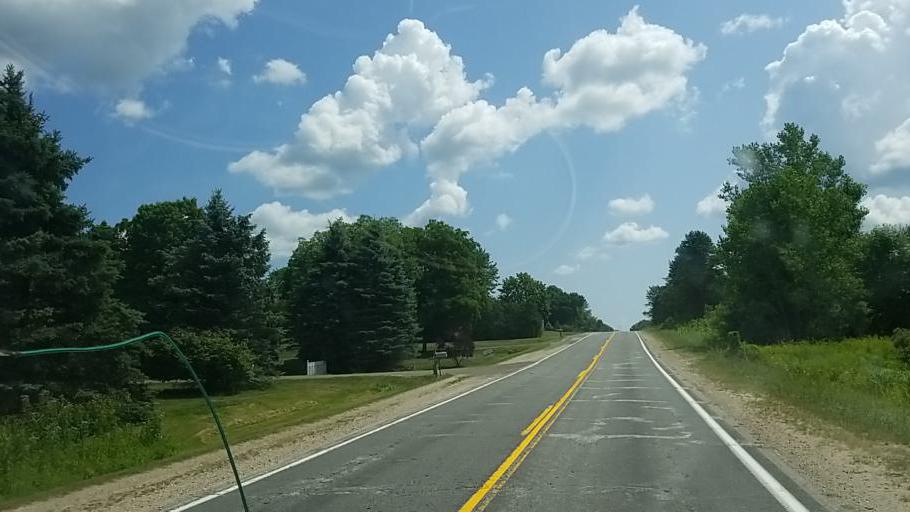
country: US
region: Michigan
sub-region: Kent County
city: Walker
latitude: 43.0739
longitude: -85.7615
